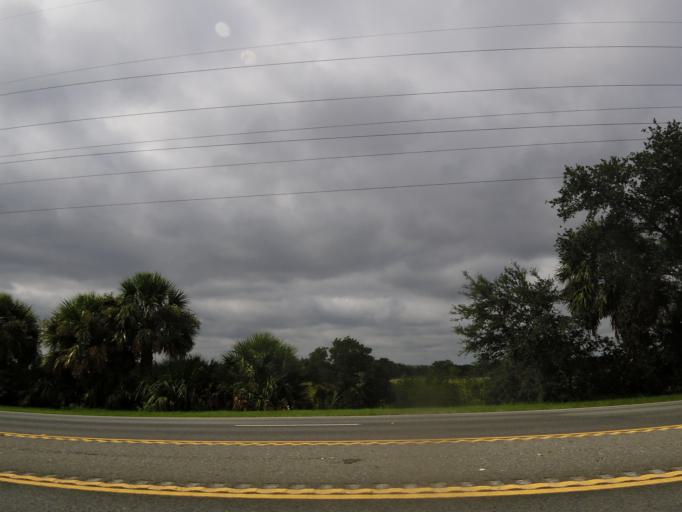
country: US
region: Georgia
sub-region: Glynn County
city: Brunswick
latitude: 31.1614
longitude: -81.4717
